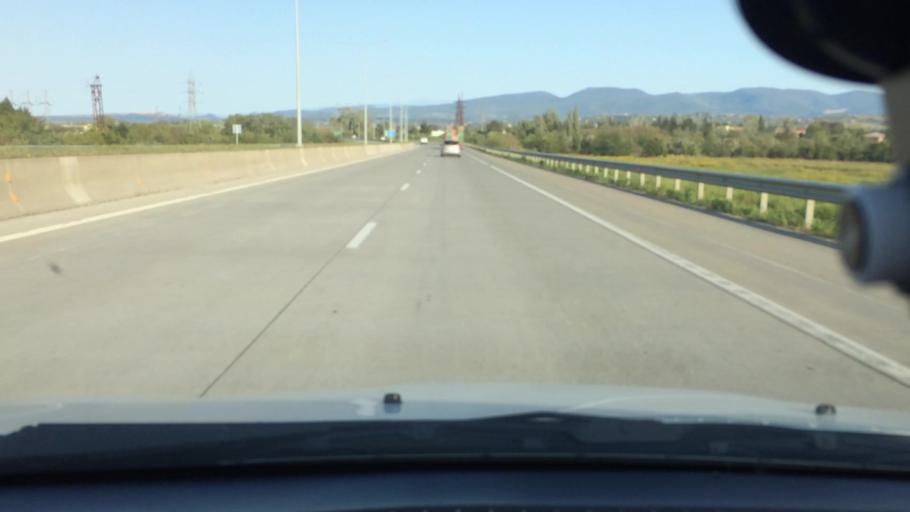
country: GE
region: Imereti
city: Zestap'oni
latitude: 42.1516
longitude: 42.9600
